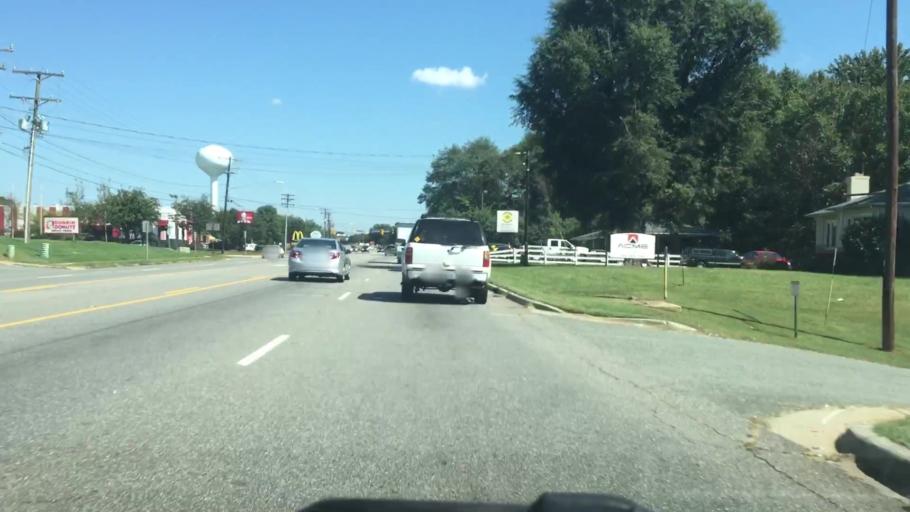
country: US
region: North Carolina
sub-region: Iredell County
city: Mooresville
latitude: 35.5940
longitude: -80.8187
